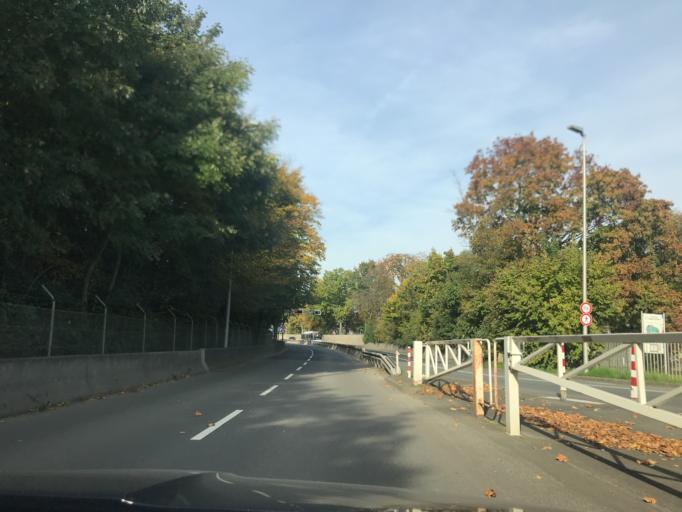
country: DE
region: North Rhine-Westphalia
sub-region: Regierungsbezirk Dusseldorf
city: Dusseldorf
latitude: 51.2590
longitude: 6.7323
